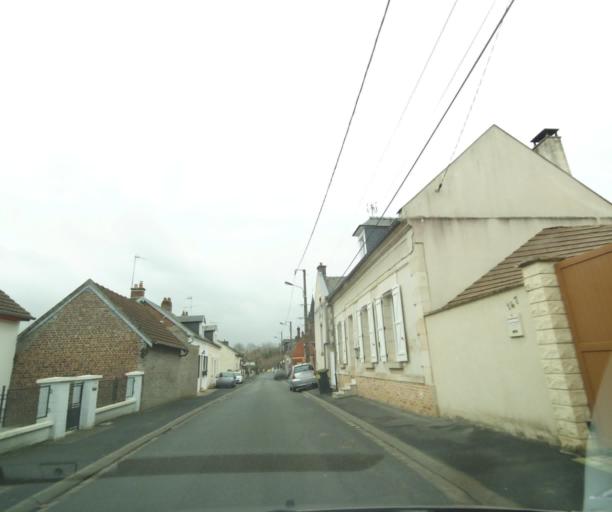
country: FR
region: Picardie
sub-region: Departement de l'Oise
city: Crisolles
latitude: 49.5995
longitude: 3.0178
